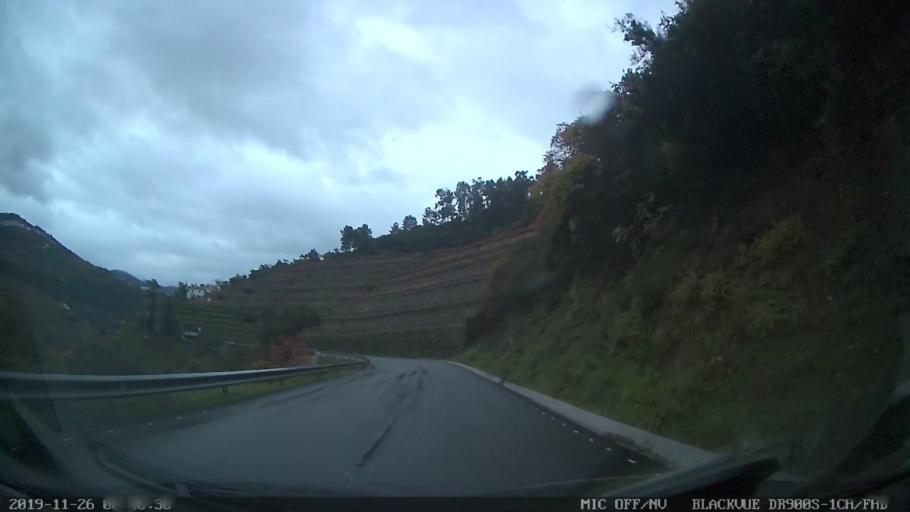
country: PT
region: Vila Real
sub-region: Sabrosa
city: Vilela
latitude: 41.1992
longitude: -7.5596
